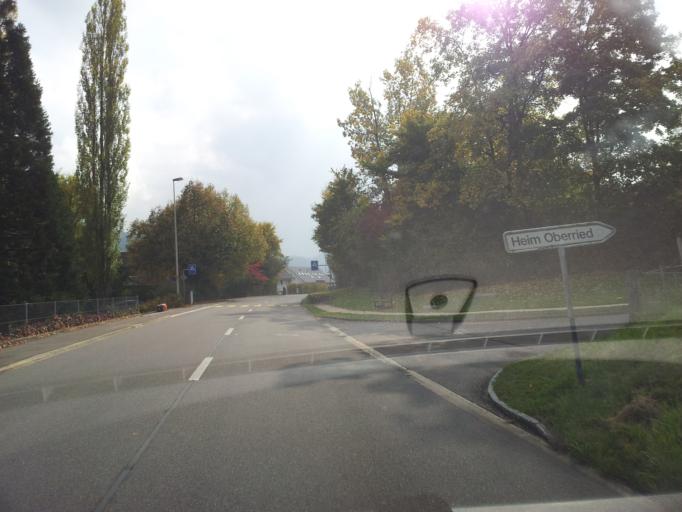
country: CH
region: Bern
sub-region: Bern-Mittelland District
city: Belp
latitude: 46.8898
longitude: 7.4953
